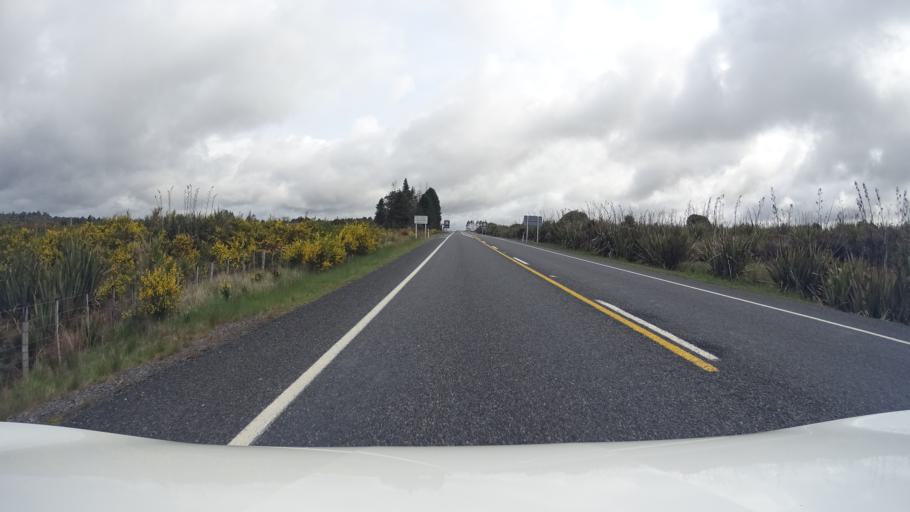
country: NZ
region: Manawatu-Wanganui
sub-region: Ruapehu District
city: Waiouru
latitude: -39.1800
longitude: 175.4023
